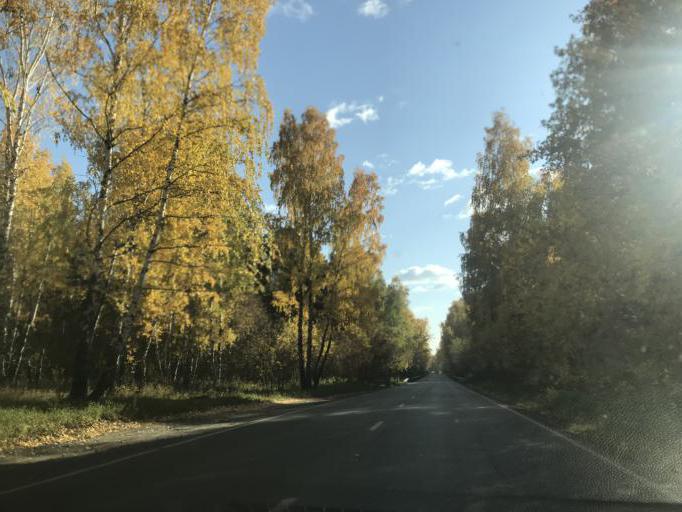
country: RU
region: Chelyabinsk
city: Dolgoderevenskoye
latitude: 55.2692
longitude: 61.3649
